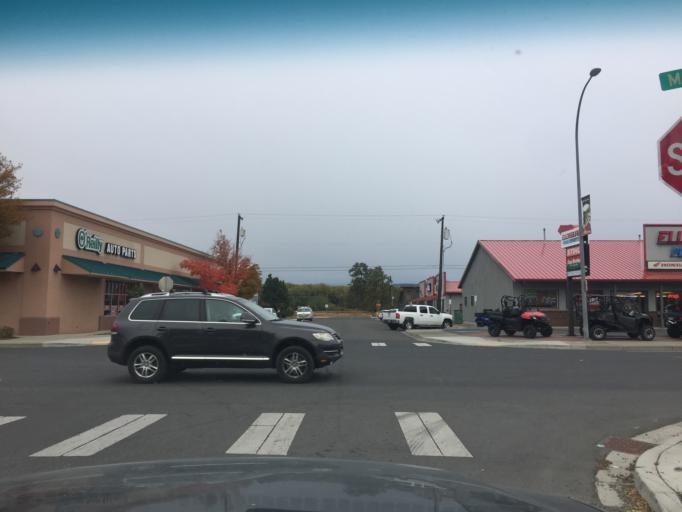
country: US
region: Washington
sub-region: Kittitas County
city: Ellensburg
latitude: 46.9893
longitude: -120.5481
